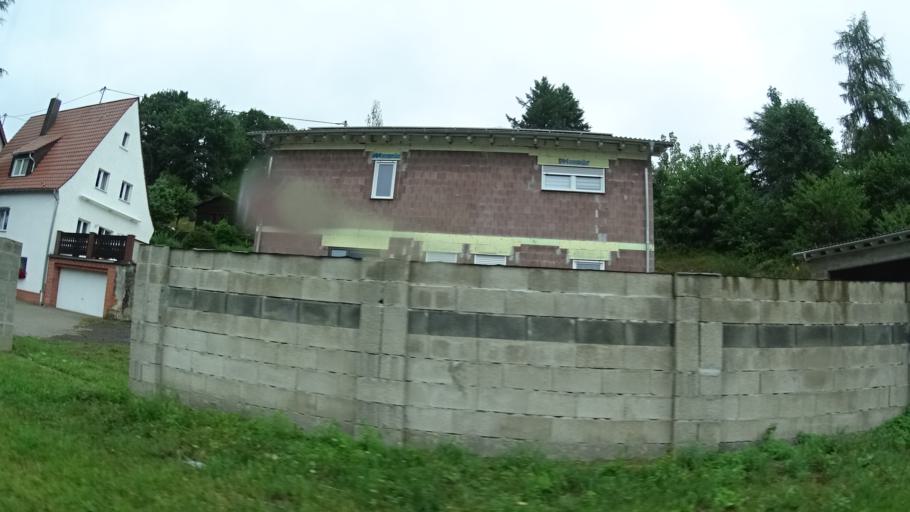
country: DE
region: Saarland
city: Hangard
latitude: 49.3530
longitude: 7.2088
